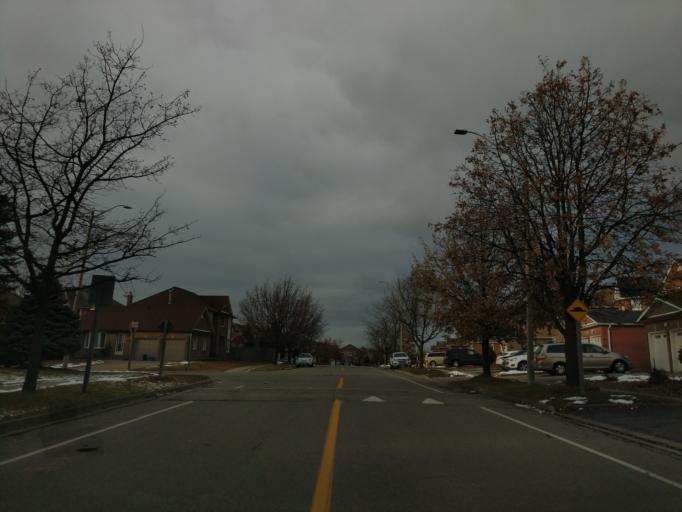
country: CA
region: Ontario
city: Markham
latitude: 43.8452
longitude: -79.2694
